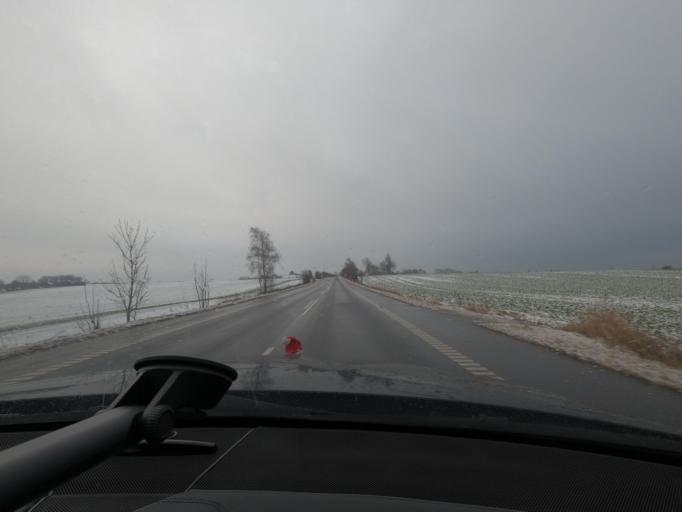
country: DK
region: South Denmark
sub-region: Sonderborg Kommune
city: Horuphav
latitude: 54.9041
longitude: 9.9437
